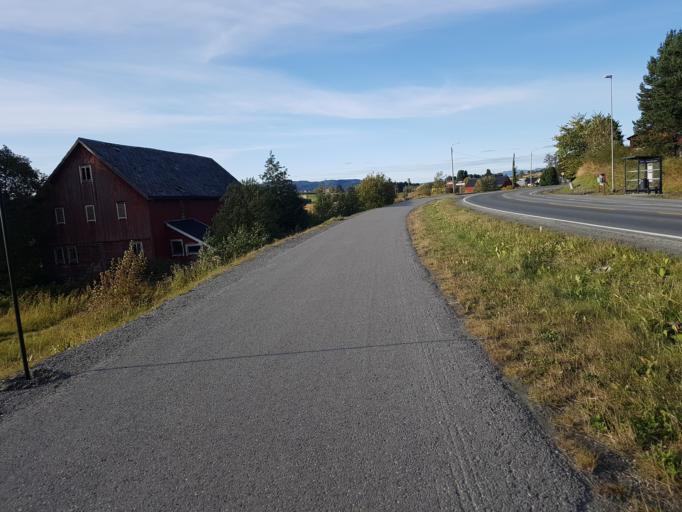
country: NO
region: Sor-Trondelag
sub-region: Trondheim
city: Trondheim
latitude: 63.3735
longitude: 10.4307
